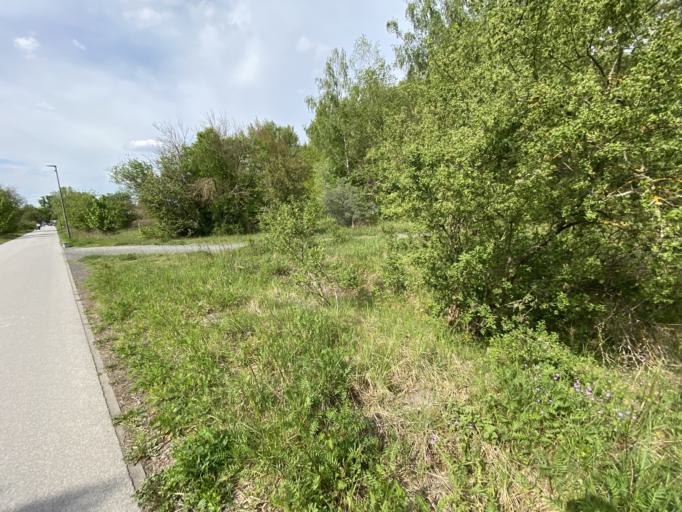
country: DE
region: Bavaria
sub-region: Regierungsbezirk Mittelfranken
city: Erlangen
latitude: 49.5837
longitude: 11.0256
